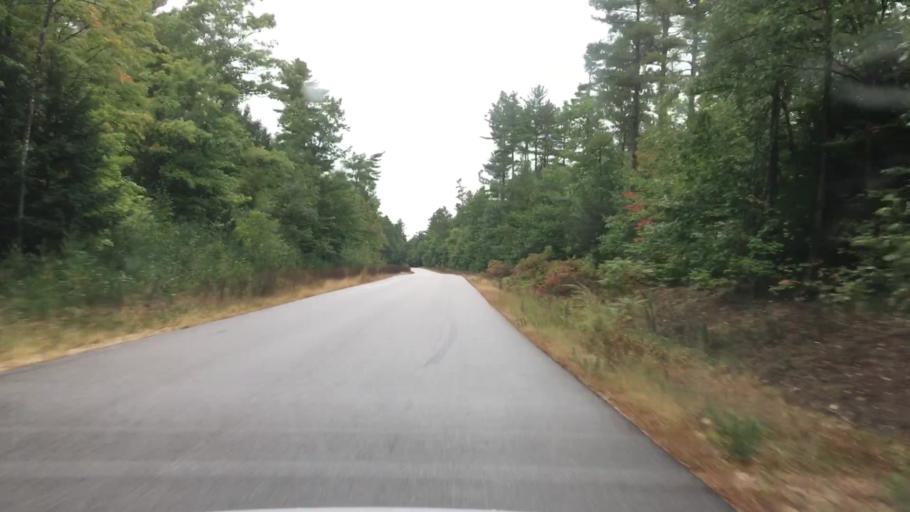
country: US
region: Maine
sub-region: Cumberland County
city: Harrison
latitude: 44.0276
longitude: -70.5936
